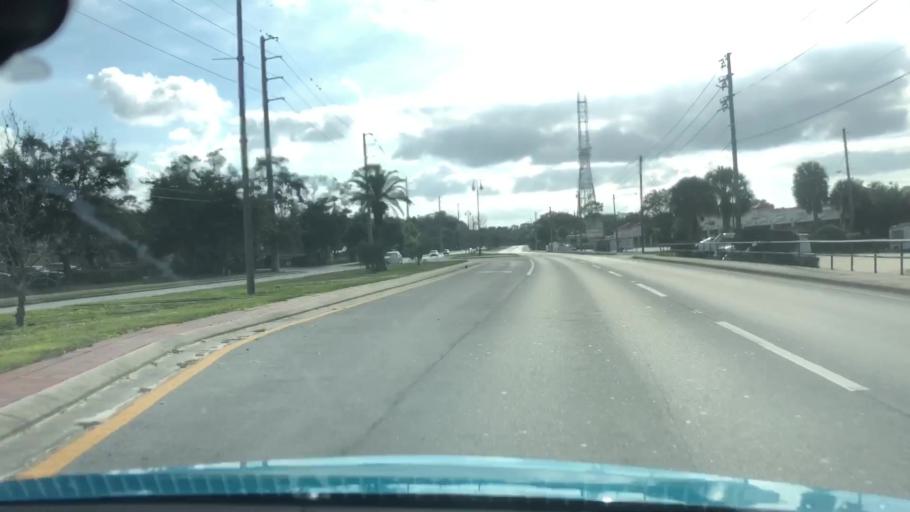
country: US
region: Florida
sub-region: Seminole County
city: Longwood
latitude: 28.7187
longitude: -81.3387
